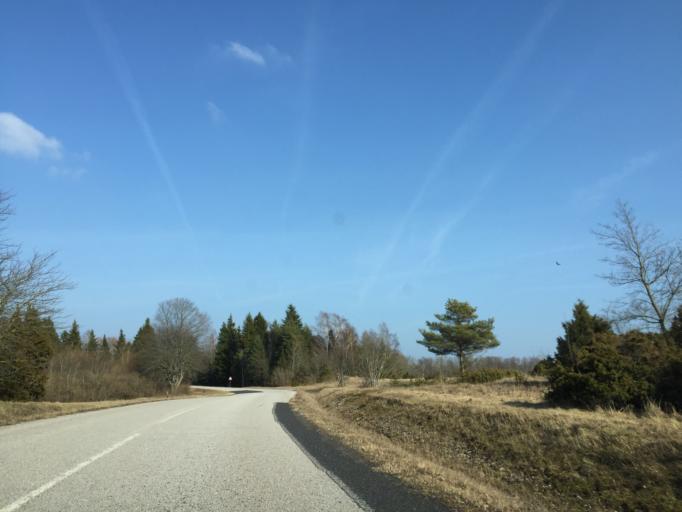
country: EE
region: Saare
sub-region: Kuressaare linn
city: Kuressaare
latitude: 58.0467
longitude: 22.1233
